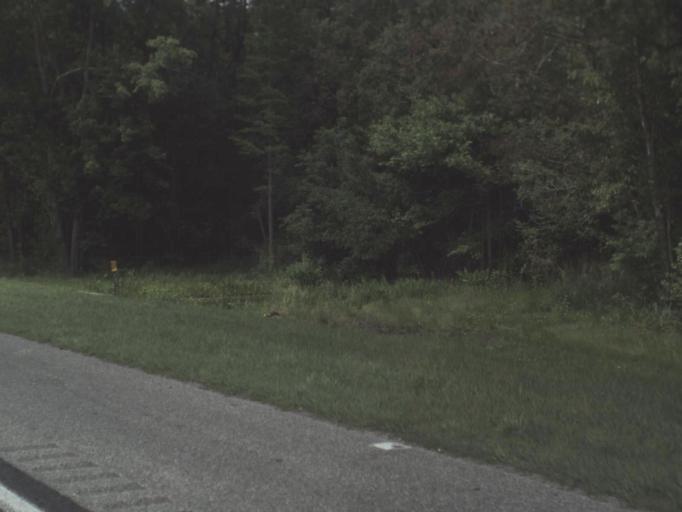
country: US
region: Florida
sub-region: Saint Johns County
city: Villano Beach
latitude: 29.9998
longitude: -81.4699
